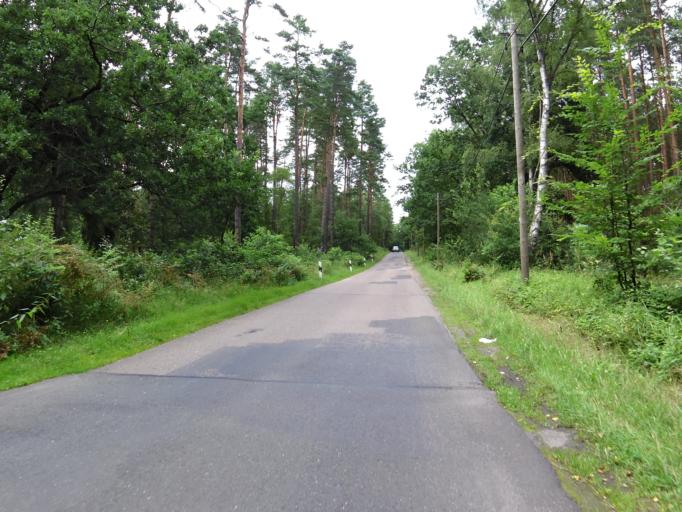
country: DE
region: Brandenburg
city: Furstenberg
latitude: 53.2021
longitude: 13.1723
